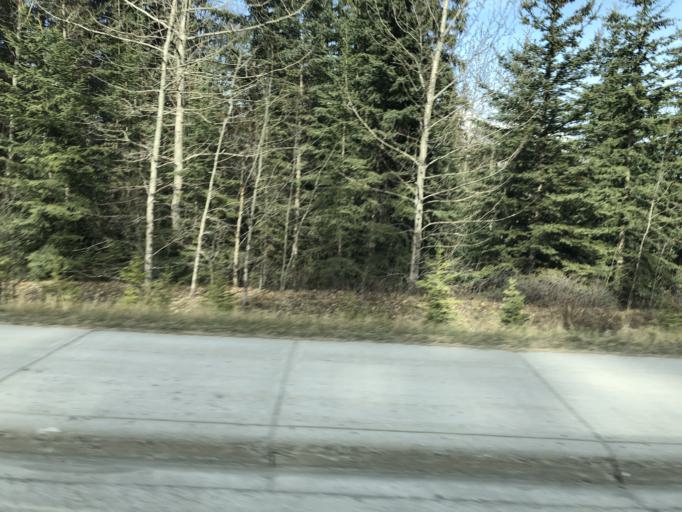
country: CA
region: Alberta
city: Canmore
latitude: 51.0755
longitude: -115.3655
